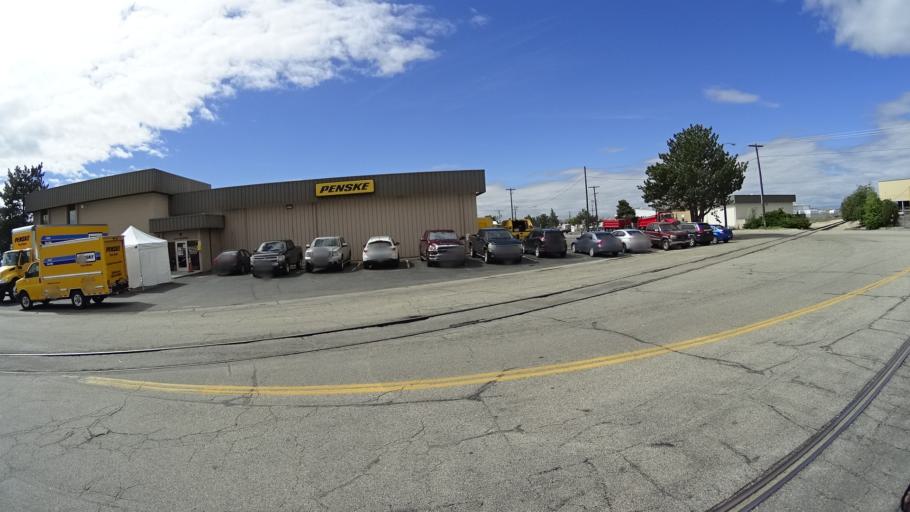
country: US
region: Idaho
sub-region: Ada County
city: Boise
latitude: 43.5625
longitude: -116.1982
